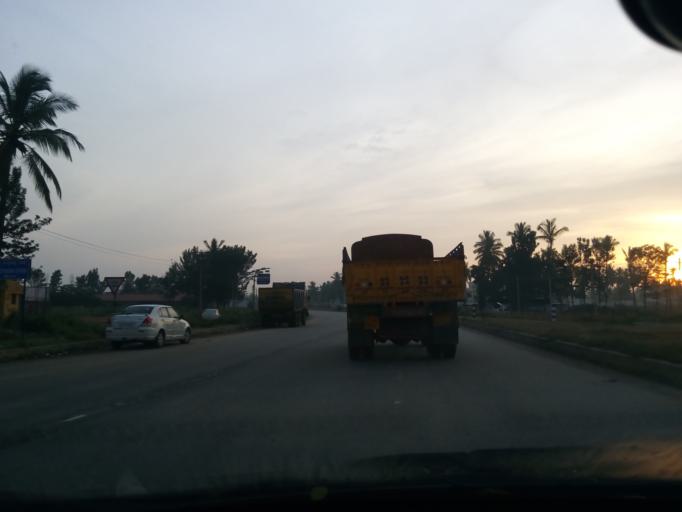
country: IN
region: Karnataka
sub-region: Bangalore Rural
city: Devanhalli
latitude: 13.2427
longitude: 77.7041
